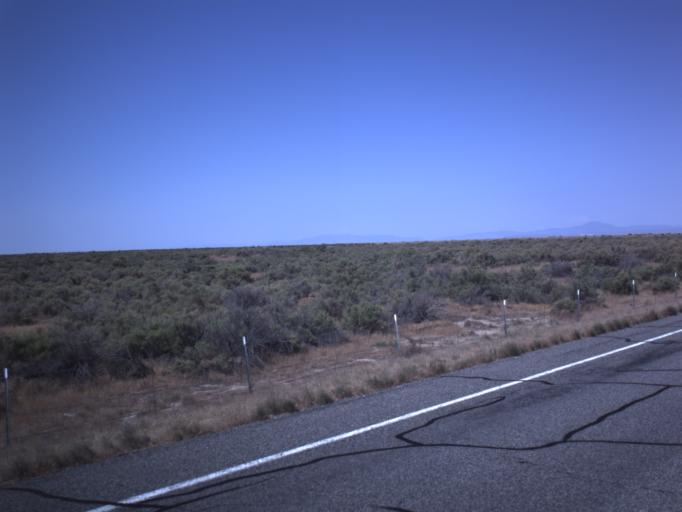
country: US
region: Utah
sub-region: Millard County
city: Delta
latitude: 39.4674
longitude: -112.4466
